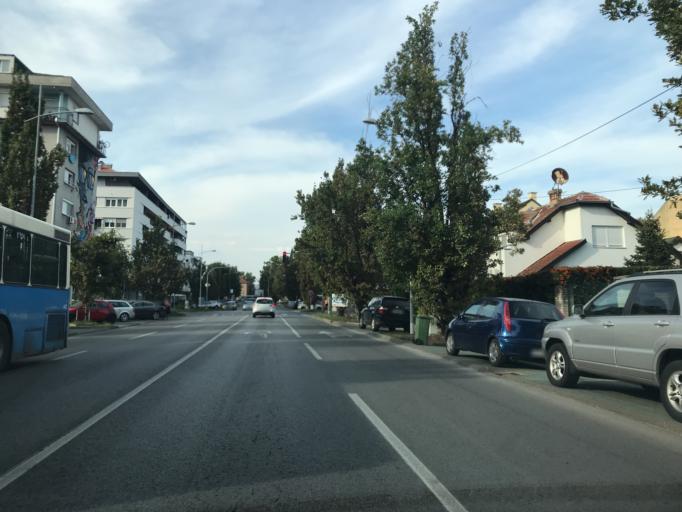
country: RS
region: Autonomna Pokrajina Vojvodina
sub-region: Juznobacki Okrug
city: Novi Sad
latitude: 45.2466
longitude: 19.8251
